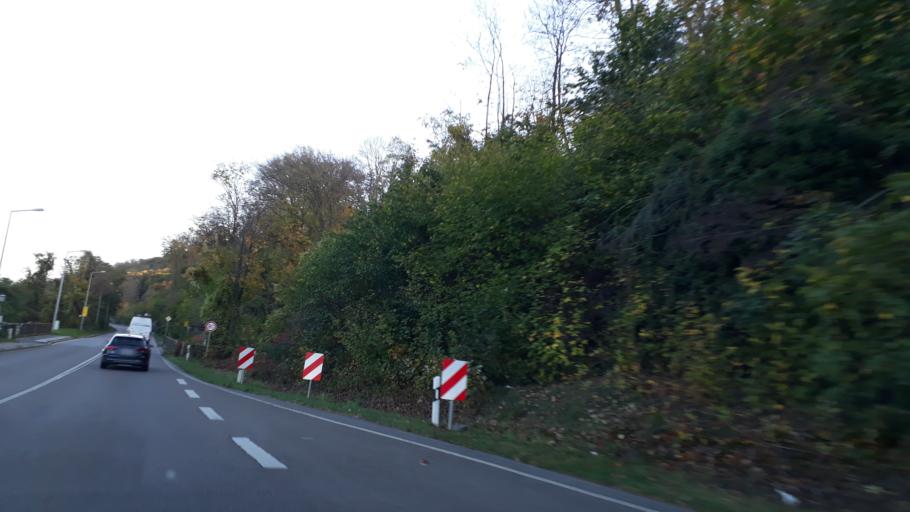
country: DE
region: Saxony
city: Coswig
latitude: 51.0911
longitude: 13.6079
